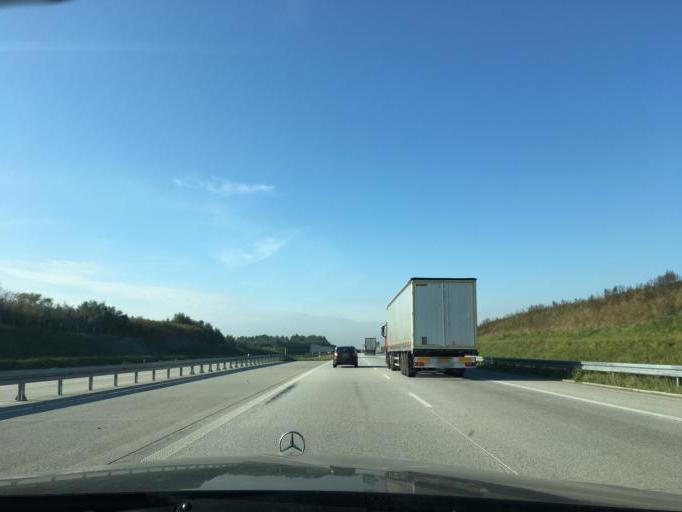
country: PL
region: Lodz Voivodeship
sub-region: Powiat lodzki wschodni
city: Andrespol
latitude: 51.8183
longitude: 19.6433
